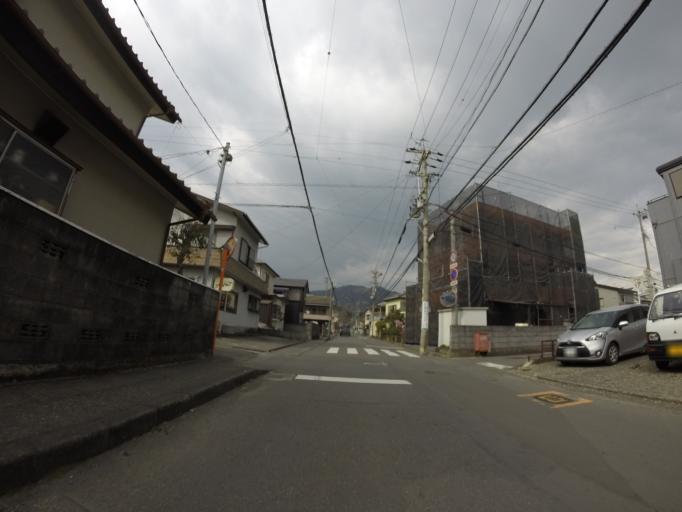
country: JP
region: Shizuoka
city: Shizuoka-shi
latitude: 35.0359
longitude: 138.4499
